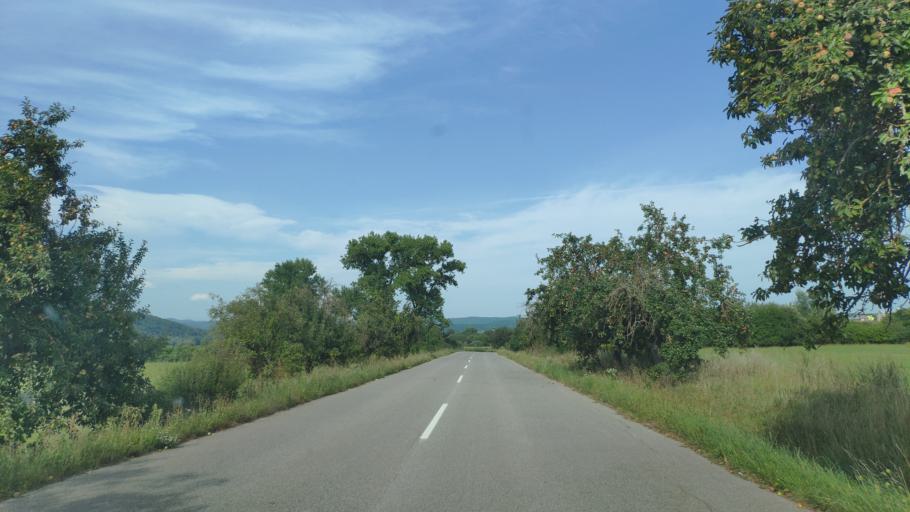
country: HU
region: Borsod-Abauj-Zemplen
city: Putnok
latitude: 48.4782
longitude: 20.3555
